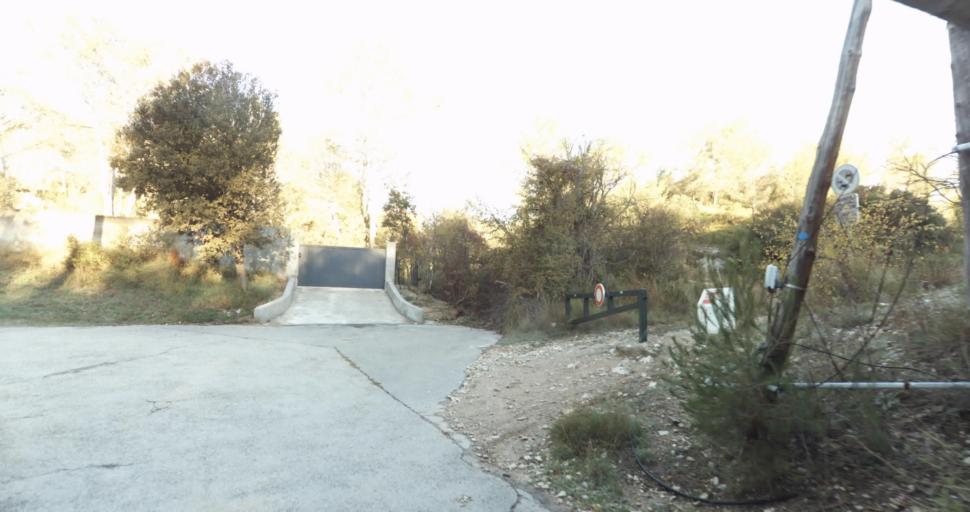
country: FR
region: Provence-Alpes-Cote d'Azur
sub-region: Departement des Bouches-du-Rhone
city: Venelles
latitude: 43.5892
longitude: 5.5089
